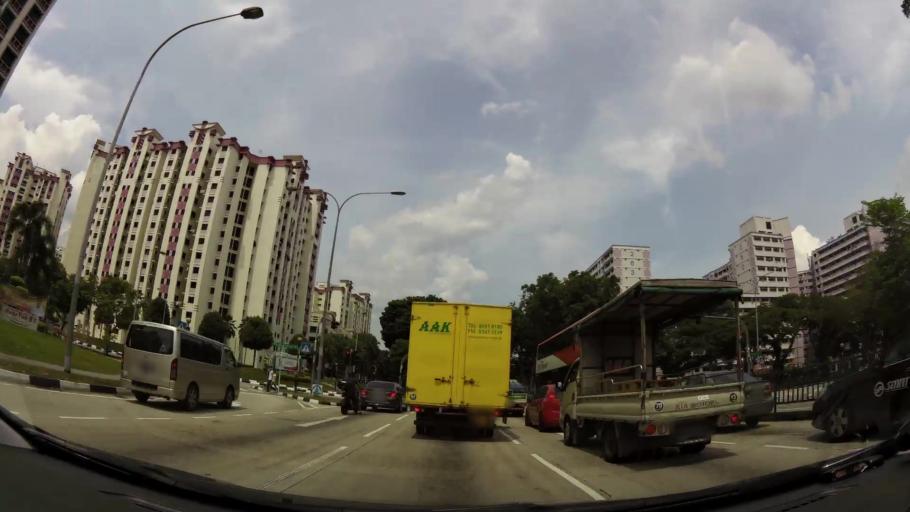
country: MY
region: Johor
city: Johor Bahru
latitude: 1.3437
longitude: 103.7073
